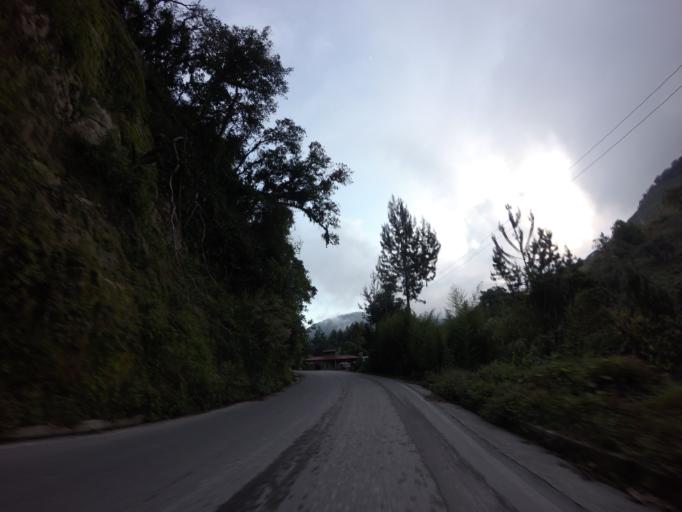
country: CO
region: Caldas
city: Manzanares
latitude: 5.2890
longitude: -75.1494
